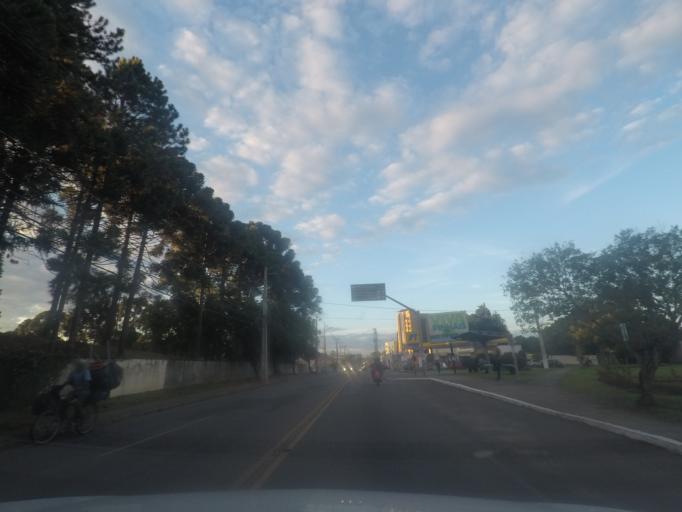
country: BR
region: Parana
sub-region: Pinhais
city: Pinhais
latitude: -25.4427
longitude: -49.1883
